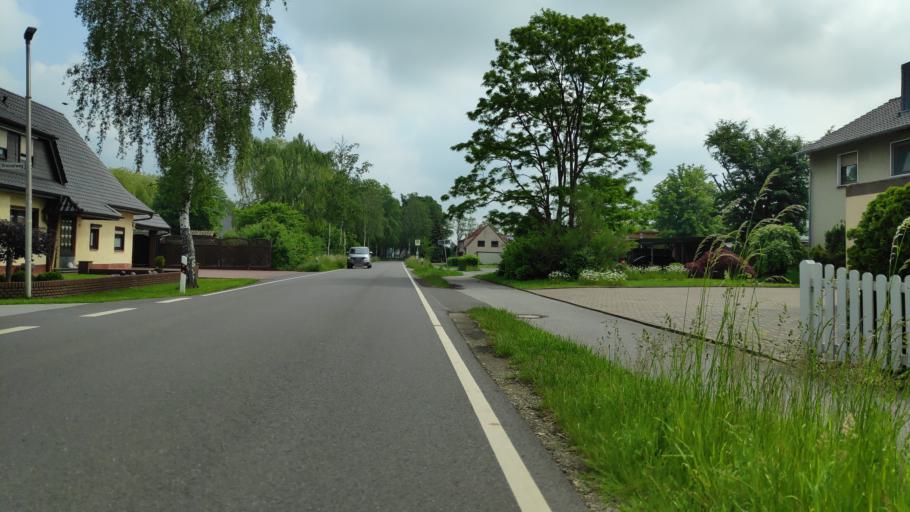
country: DE
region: North Rhine-Westphalia
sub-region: Regierungsbezirk Detmold
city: Hille
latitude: 52.3673
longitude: 8.7643
